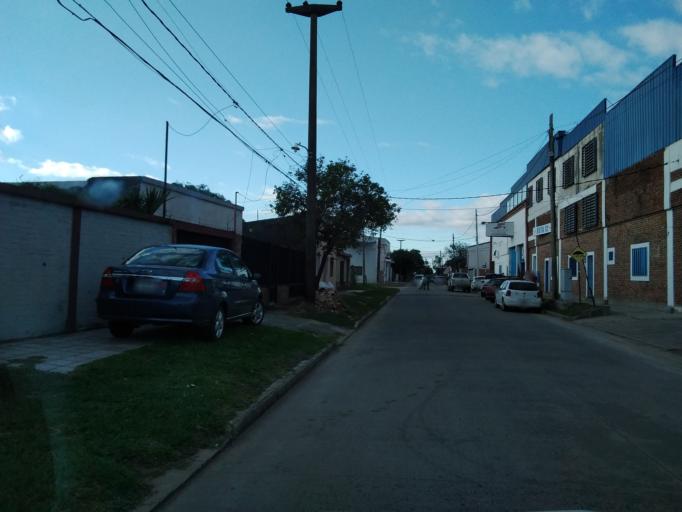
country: AR
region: Corrientes
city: Corrientes
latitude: -27.4757
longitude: -58.8057
